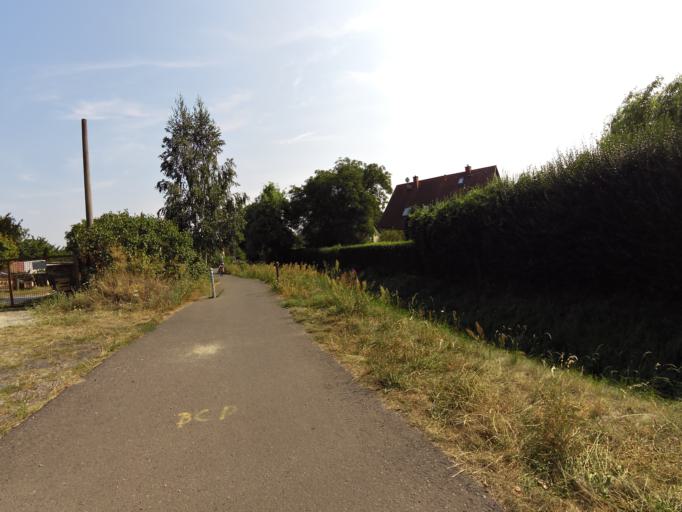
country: DE
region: Berlin
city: Adlershof
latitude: 52.4231
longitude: 13.5464
